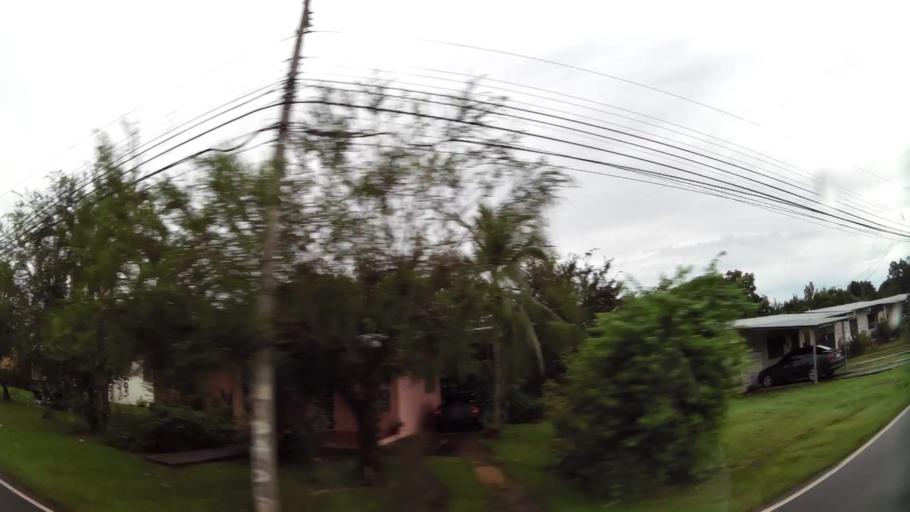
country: PA
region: Veraguas
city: Santiago de Veraguas
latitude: 8.1217
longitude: -80.9690
